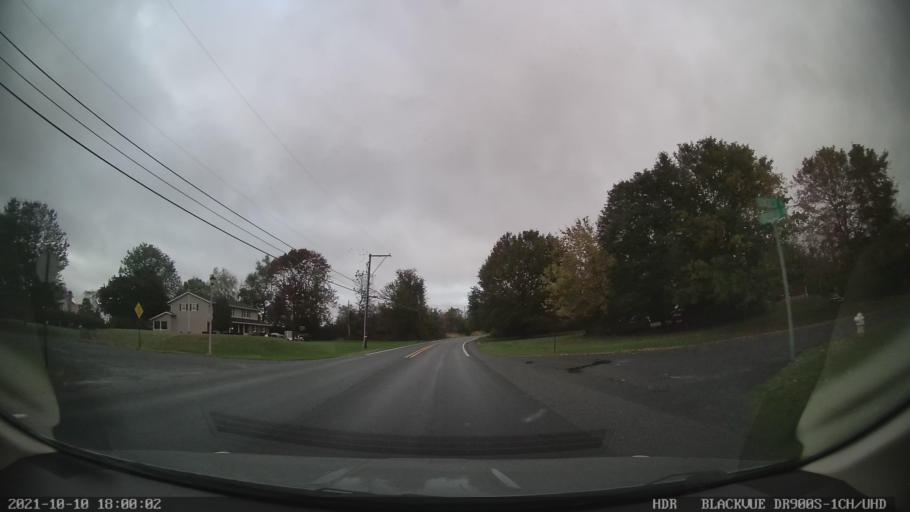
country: US
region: Pennsylvania
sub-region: Lehigh County
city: Egypt
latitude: 40.6430
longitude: -75.5524
